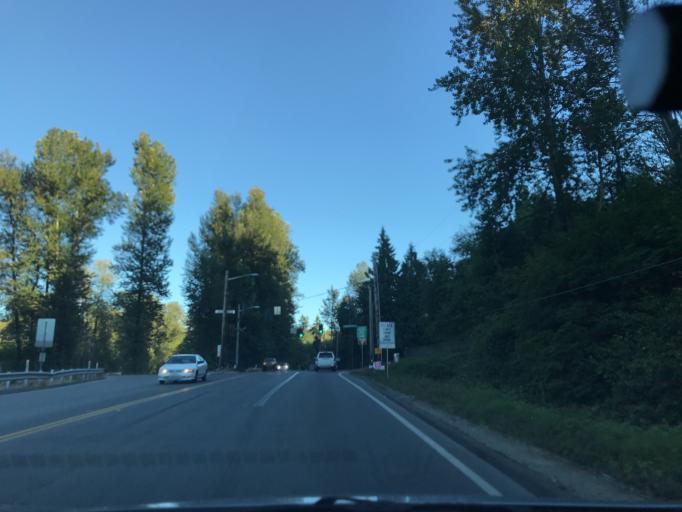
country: US
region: Washington
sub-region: King County
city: Auburn
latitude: 47.2727
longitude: -122.2074
